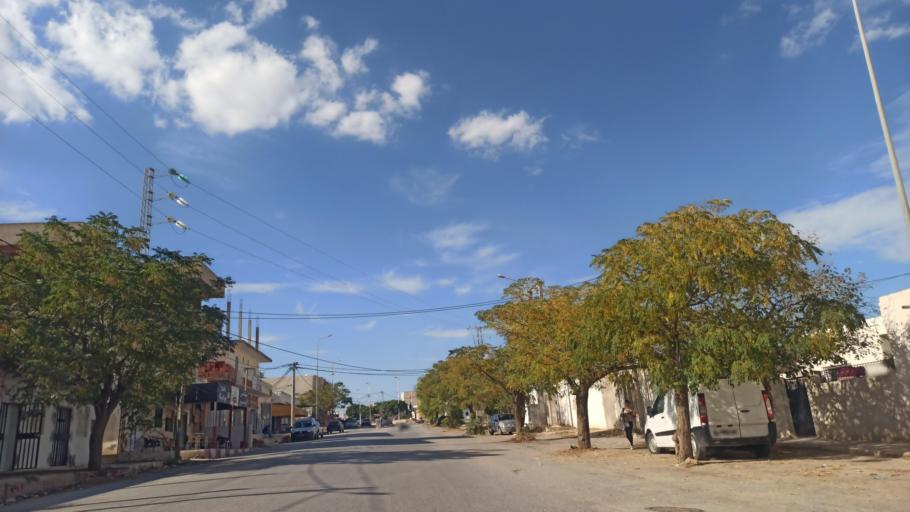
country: TN
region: Zaghwan
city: Zaghouan
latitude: 36.3482
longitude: 10.2066
